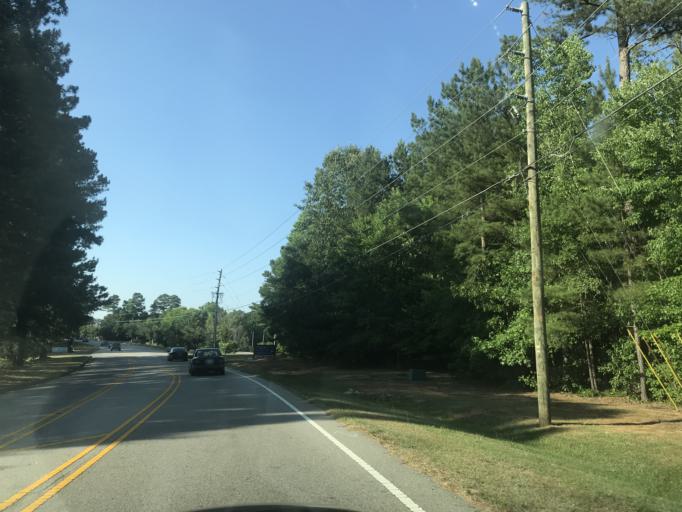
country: US
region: North Carolina
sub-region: Wake County
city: Garner
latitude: 35.7132
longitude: -78.6027
